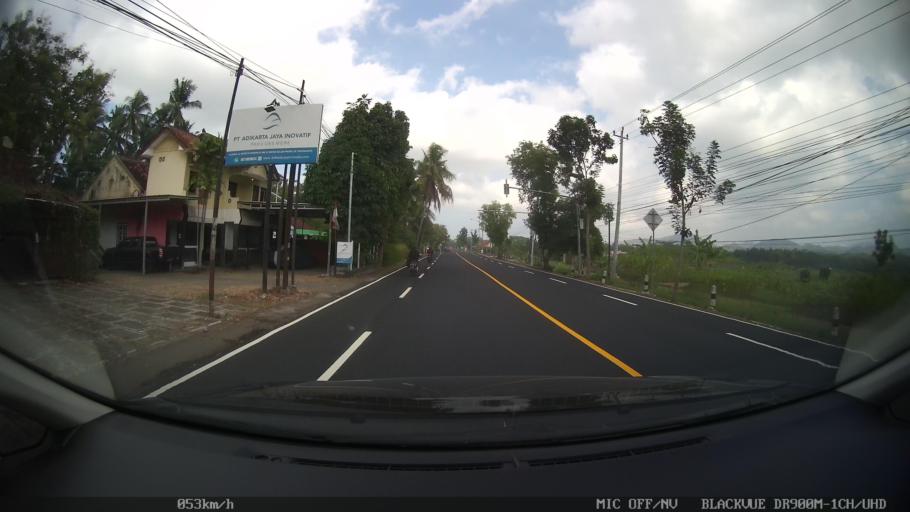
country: ID
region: Daerah Istimewa Yogyakarta
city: Srandakan
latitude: -7.8694
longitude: 110.1457
